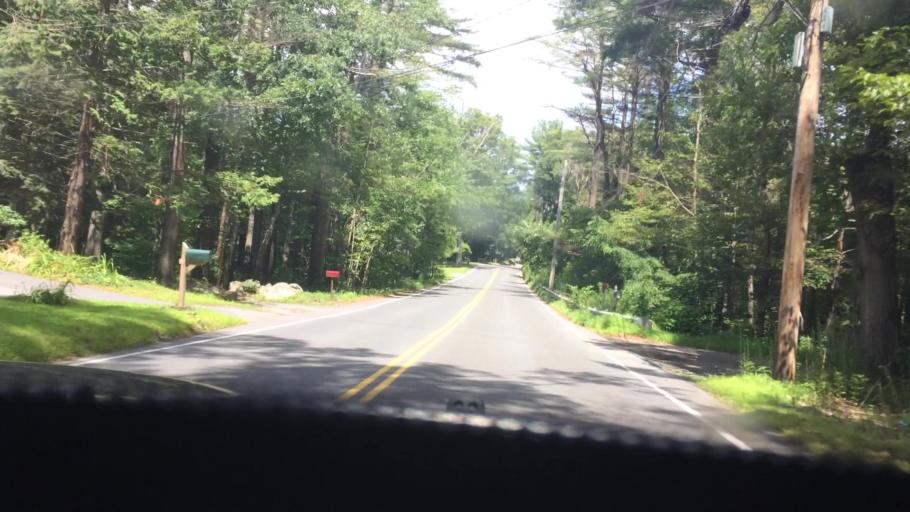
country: US
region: Massachusetts
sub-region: Middlesex County
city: Maynard
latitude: 42.4100
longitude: -71.4444
